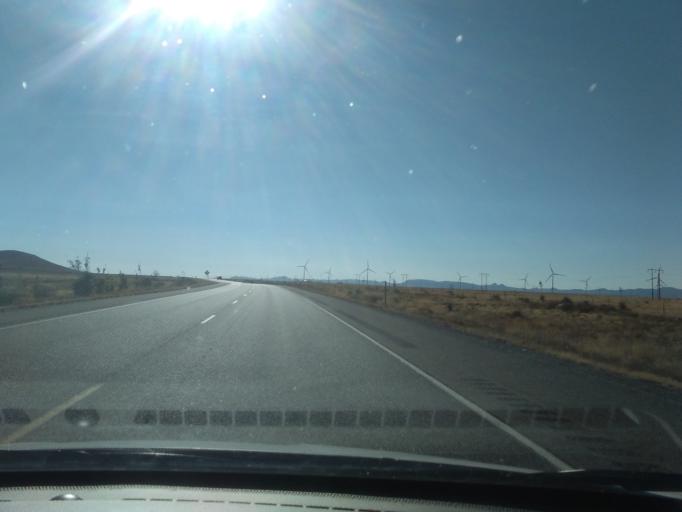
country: US
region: New Mexico
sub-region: Dona Ana County
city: Hatch
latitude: 32.5597
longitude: -107.4709
